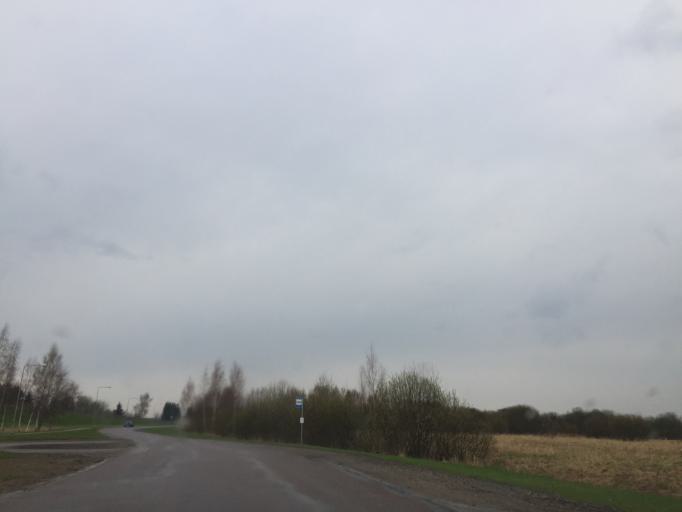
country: EE
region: Tartu
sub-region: UElenurme vald
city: Ulenurme
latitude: 58.3056
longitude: 26.7237
